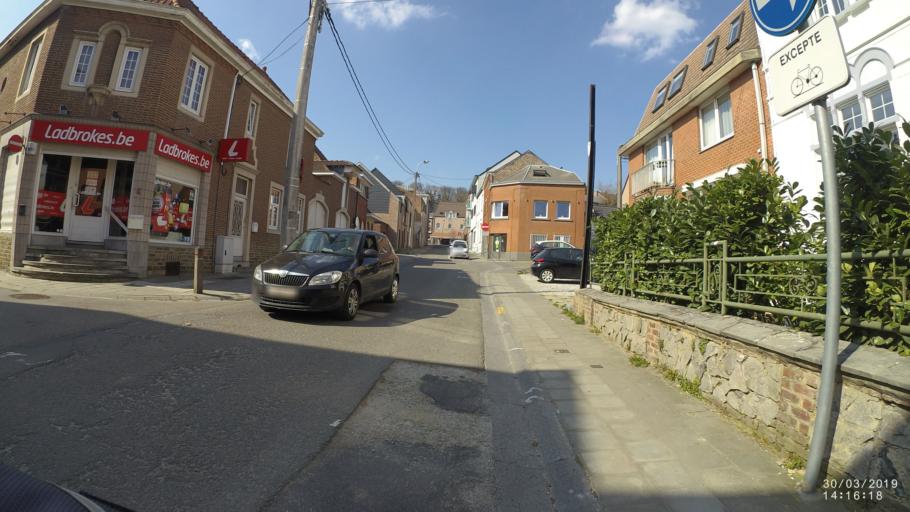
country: BE
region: Wallonia
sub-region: Province du Brabant Wallon
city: Ottignies
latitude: 50.6932
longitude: 4.5754
